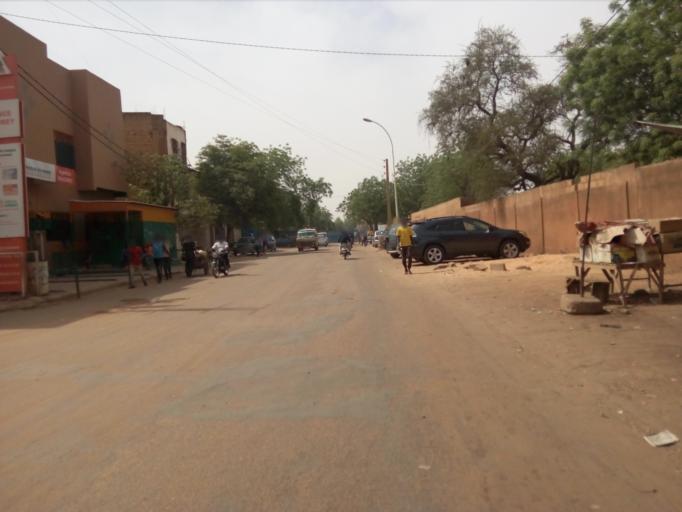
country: NE
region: Niamey
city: Niamey
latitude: 13.5180
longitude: 2.1119
